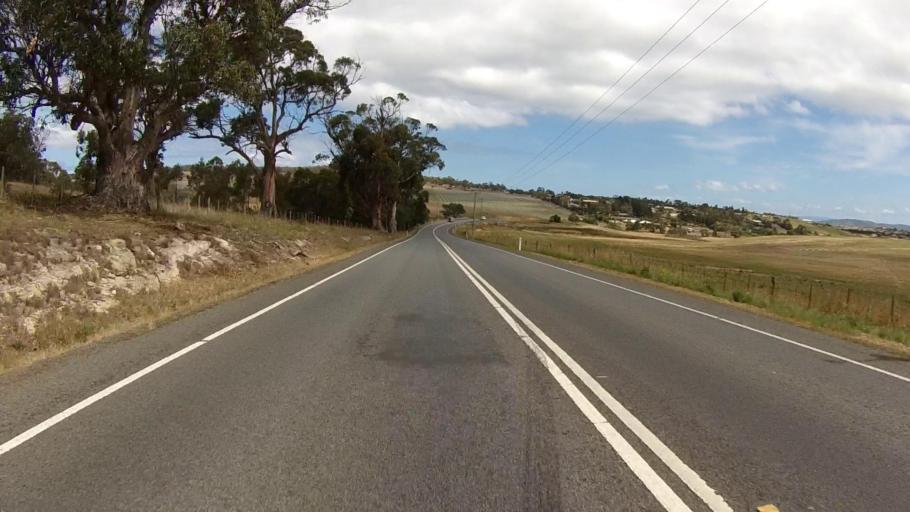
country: AU
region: Tasmania
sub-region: Sorell
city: Sorell
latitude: -42.8076
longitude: 147.6288
